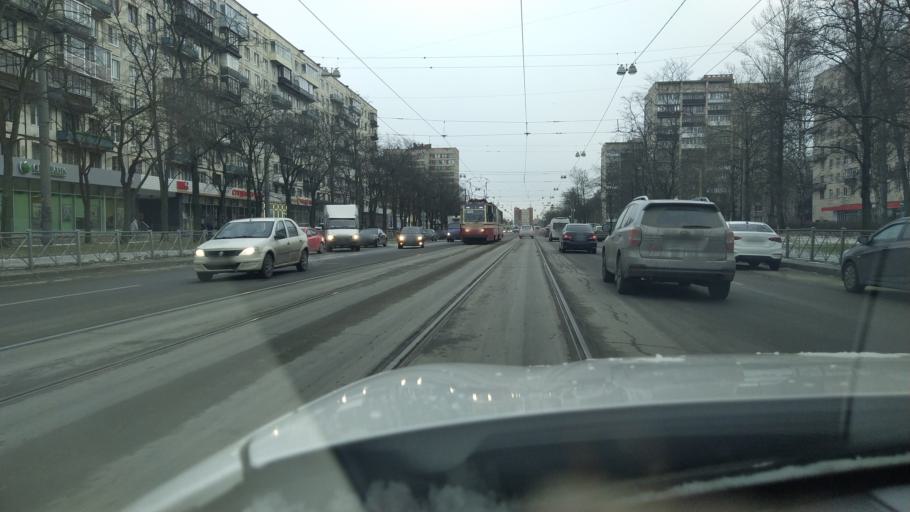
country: RU
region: Leningrad
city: Akademicheskoe
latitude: 60.0082
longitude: 30.4168
